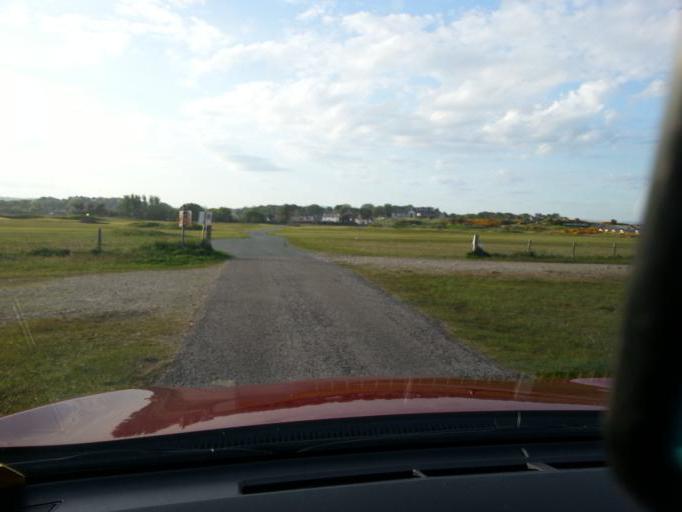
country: GB
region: Scotland
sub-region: Highland
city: Dornoch
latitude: 57.8732
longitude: -4.0236
